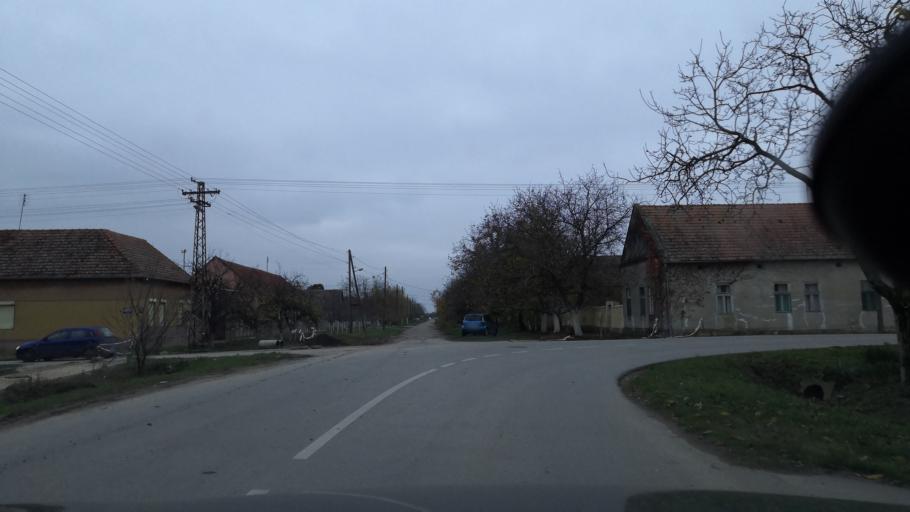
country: RS
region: Autonomna Pokrajina Vojvodina
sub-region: Severnobanatski Okrug
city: Novi Knezevac
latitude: 46.1251
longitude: 20.0985
